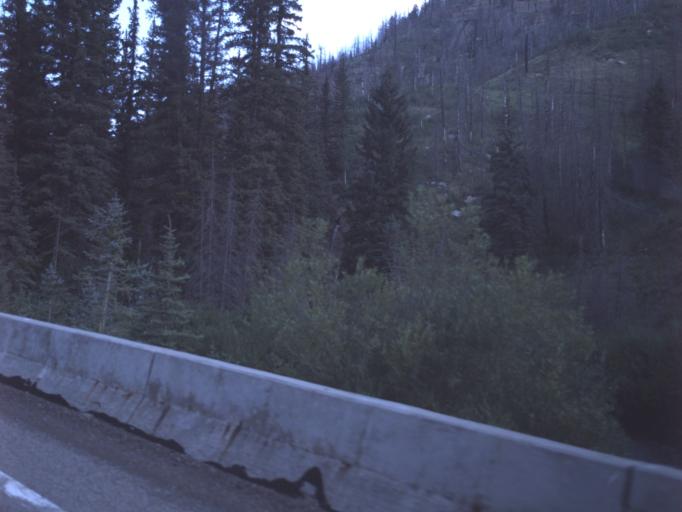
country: US
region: Utah
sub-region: Sanpete County
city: Fairview
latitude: 39.5462
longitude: -111.1652
